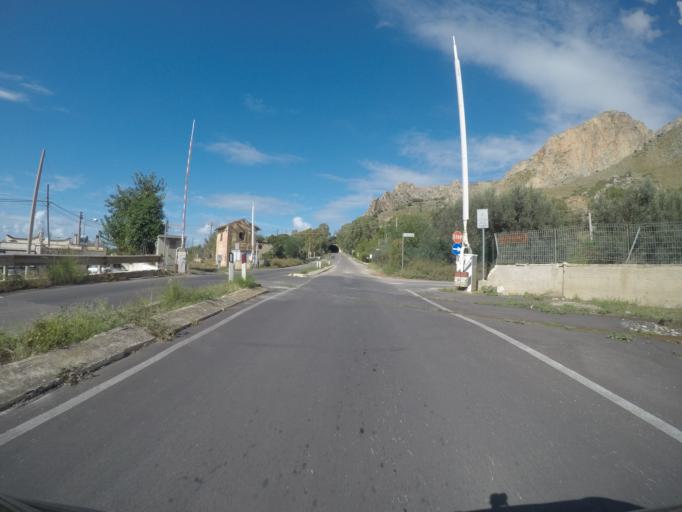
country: IT
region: Sicily
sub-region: Palermo
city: Agliandroni-Paternella
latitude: 38.1213
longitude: 13.0762
